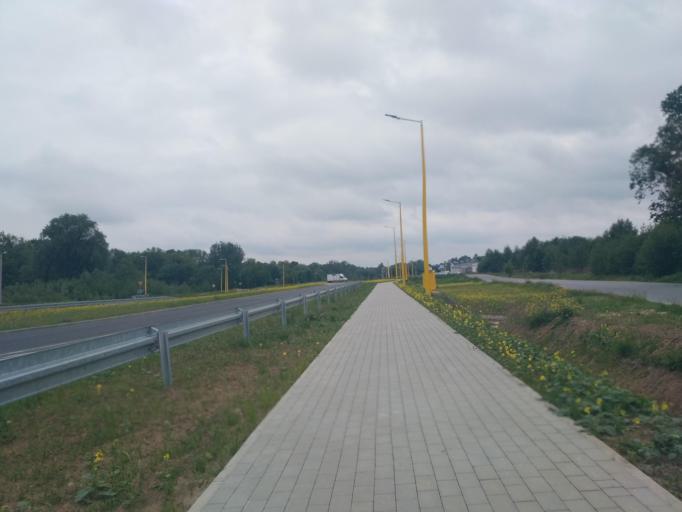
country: PL
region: Subcarpathian Voivodeship
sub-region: Krosno
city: Krosno
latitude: 49.6744
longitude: 21.7600
